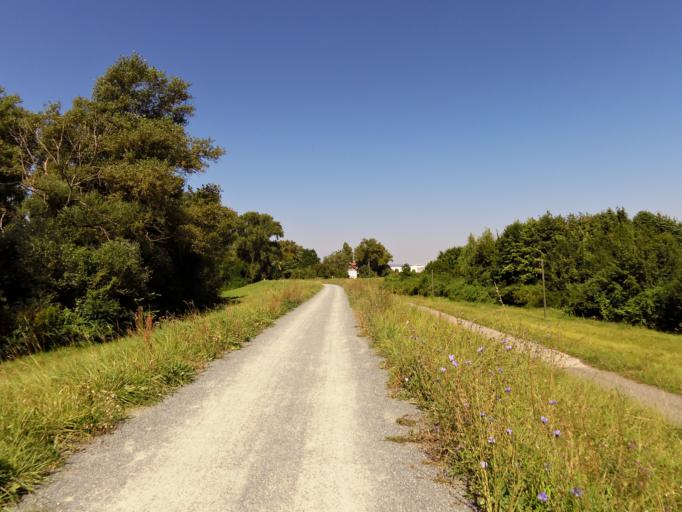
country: DE
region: Hesse
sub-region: Regierungsbezirk Darmstadt
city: Ginsheim-Gustavsburg
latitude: 49.9841
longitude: 8.3206
